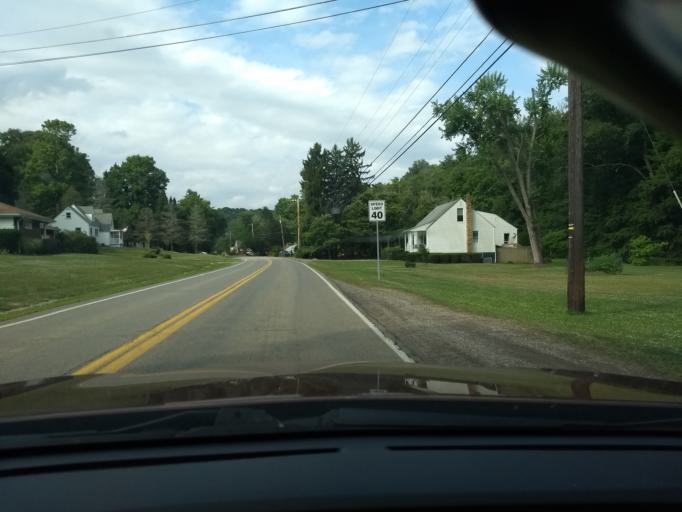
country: US
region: Pennsylvania
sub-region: Allegheny County
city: Bell Acres
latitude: 40.6179
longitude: -80.1411
